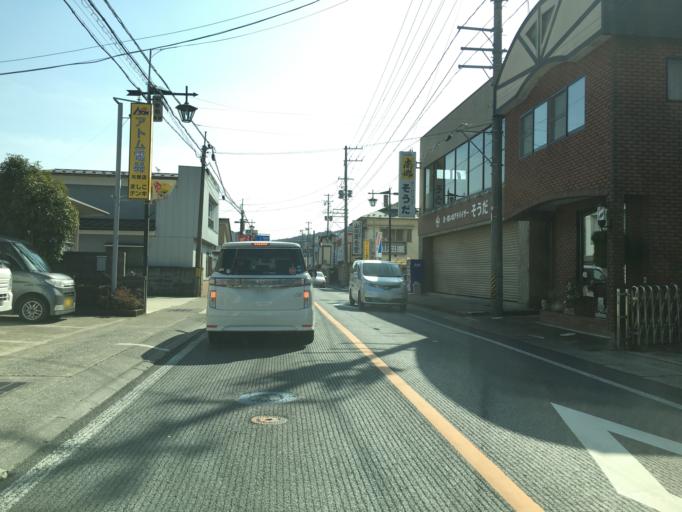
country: JP
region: Ibaraki
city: Daigo
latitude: 36.8712
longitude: 140.4244
